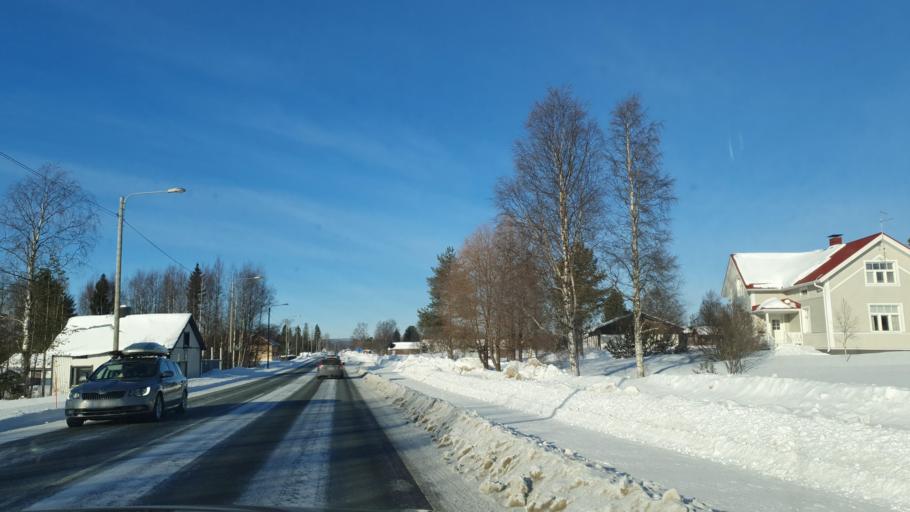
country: FI
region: Lapland
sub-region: Torniolaakso
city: Ylitornio
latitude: 66.2852
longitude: 23.6809
